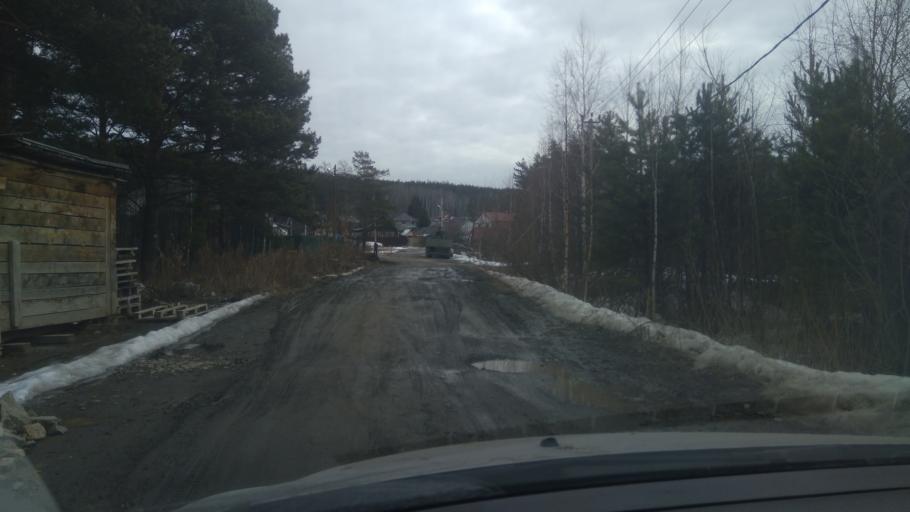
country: RU
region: Sverdlovsk
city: Severka
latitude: 56.8530
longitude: 60.3806
